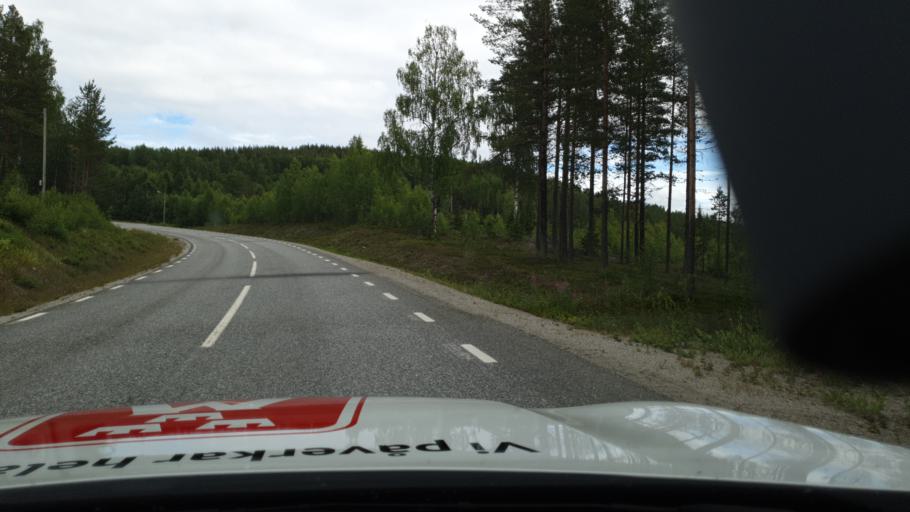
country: SE
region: Vaesterbotten
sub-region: Lycksele Kommun
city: Soderfors
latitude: 64.6175
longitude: 18.3193
